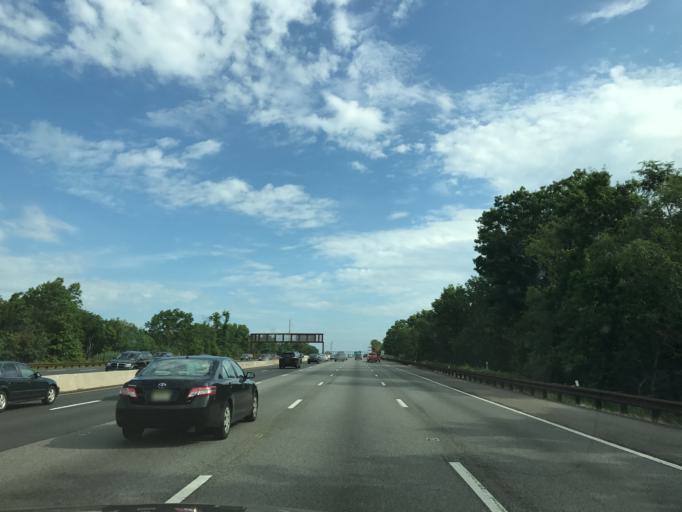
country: US
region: New Jersey
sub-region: Union County
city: Winfield
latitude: 40.6487
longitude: -74.2871
